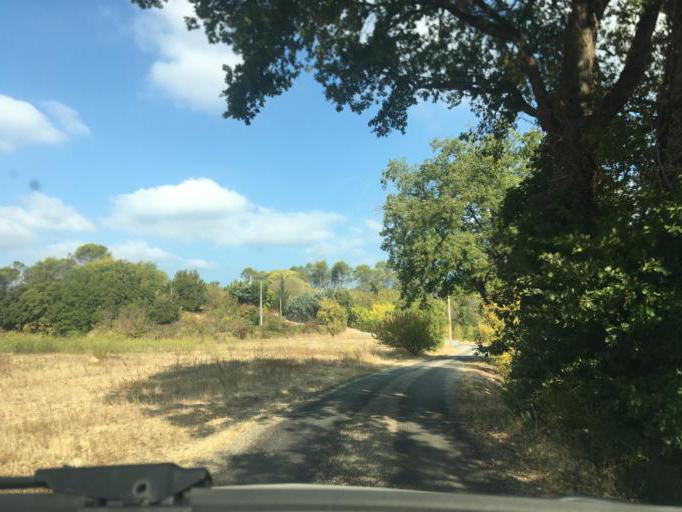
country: FR
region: Provence-Alpes-Cote d'Azur
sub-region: Departement du Var
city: Lorgues
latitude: 43.4862
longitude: 6.3999
